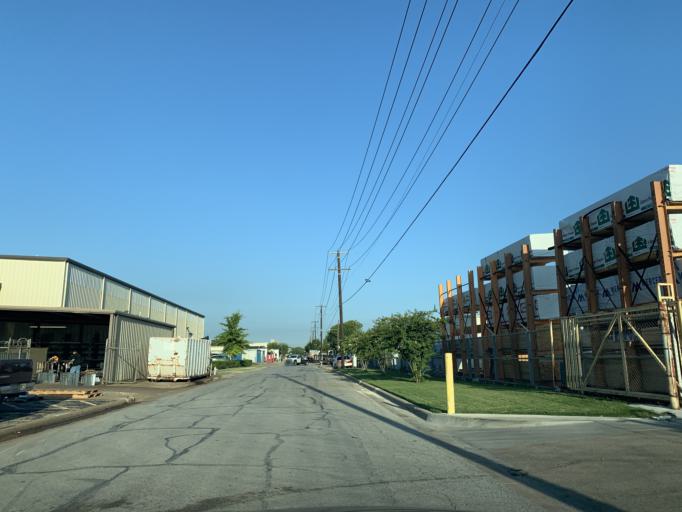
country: US
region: Texas
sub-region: Tarrant County
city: Fort Worth
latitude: 32.7581
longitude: -97.3516
